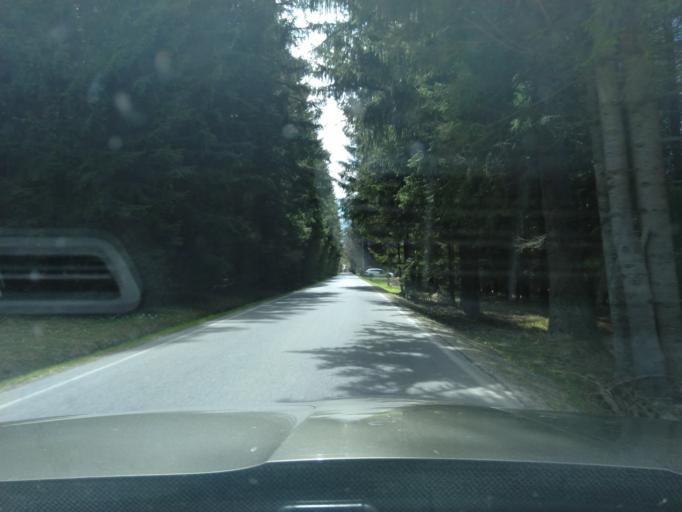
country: CZ
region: Jihocesky
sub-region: Okres Prachatice
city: Borova Lada
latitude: 49.0172
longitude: 13.6669
